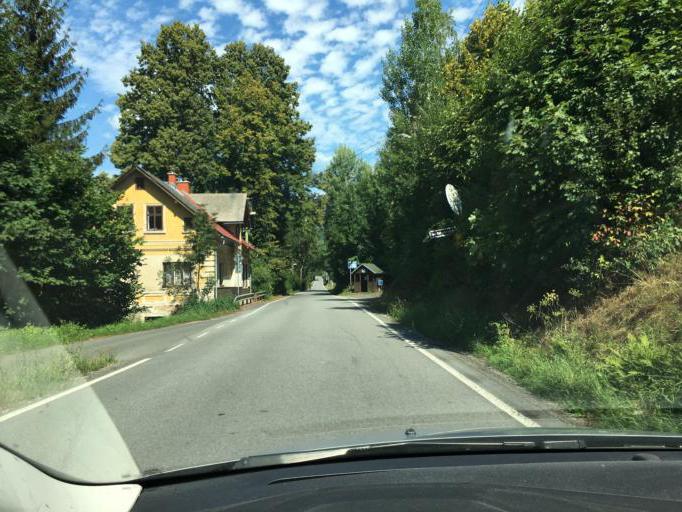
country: CZ
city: Plavy
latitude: 50.7009
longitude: 15.3567
